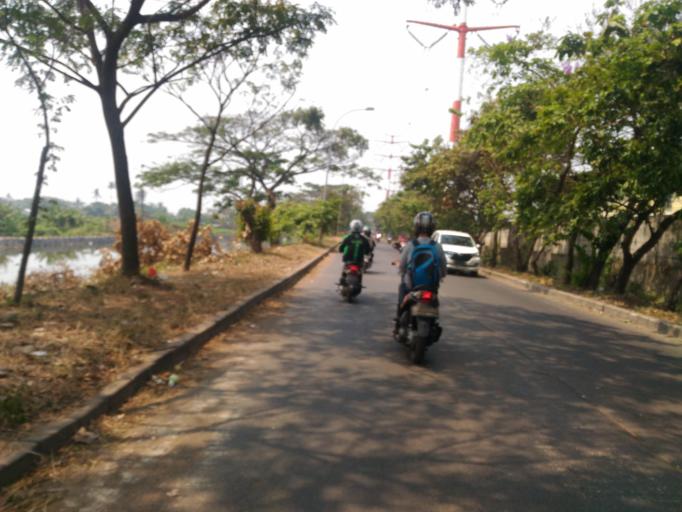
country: ID
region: West Java
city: Sepatan
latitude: -6.1489
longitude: 106.5980
